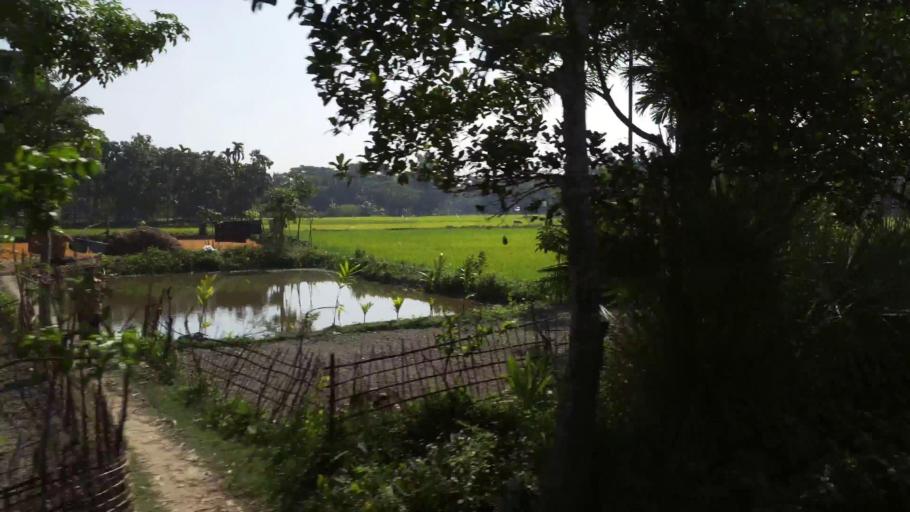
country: BD
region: Dhaka
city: Gafargaon
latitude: 24.4989
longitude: 90.5215
